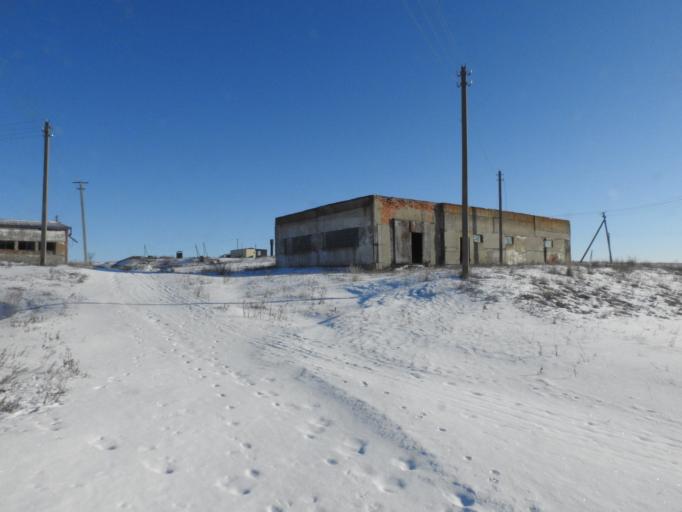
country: RU
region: Saratov
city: Lysyye Gory
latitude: 51.4311
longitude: 44.9409
